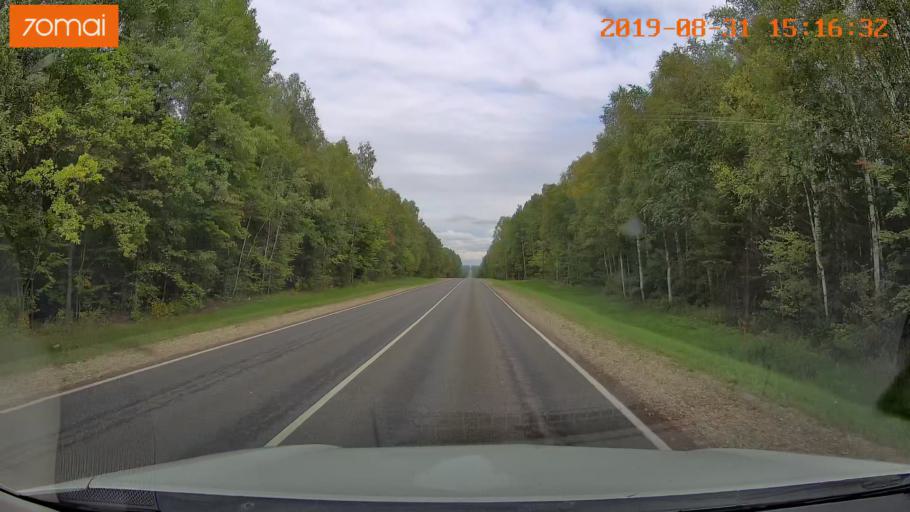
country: RU
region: Kaluga
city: Baryatino
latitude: 54.4605
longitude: 34.3521
